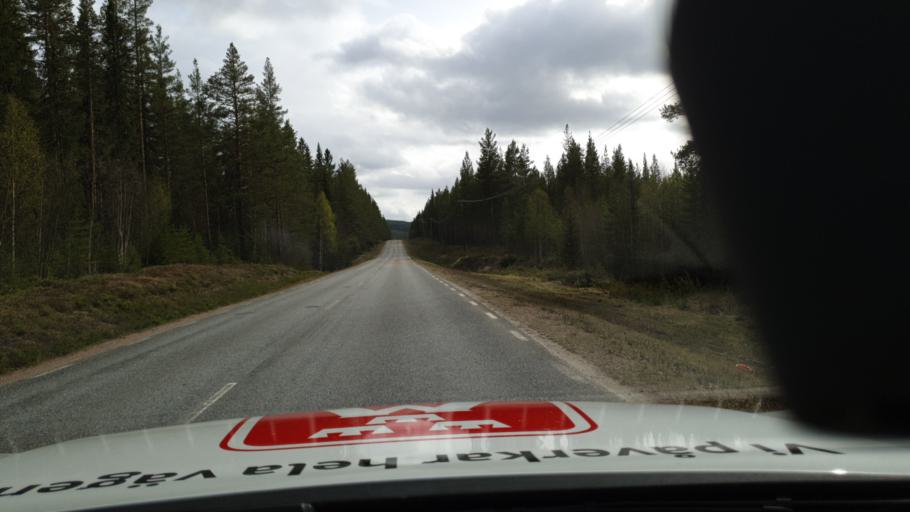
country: SE
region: Jaemtland
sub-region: Braecke Kommun
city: Braecke
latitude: 62.8403
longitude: 15.4723
